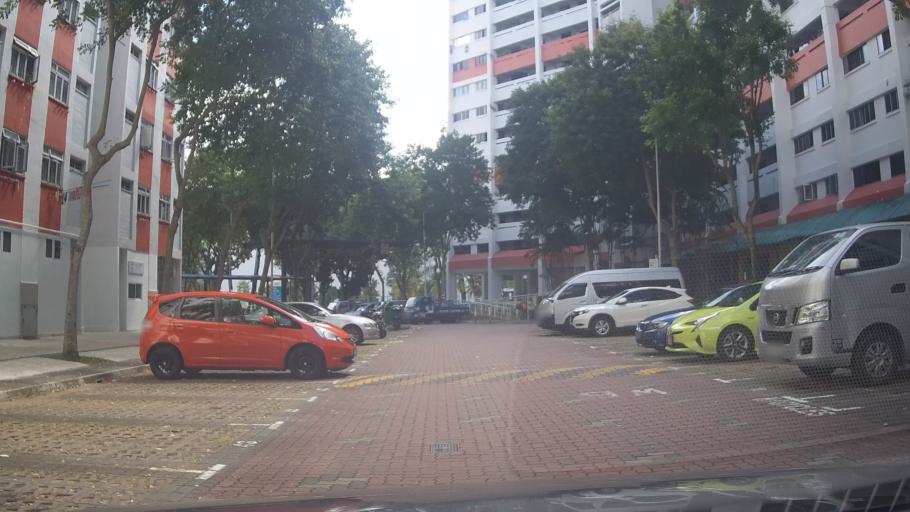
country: MY
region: Johor
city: Johor Bahru
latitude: 1.4416
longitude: 103.7778
